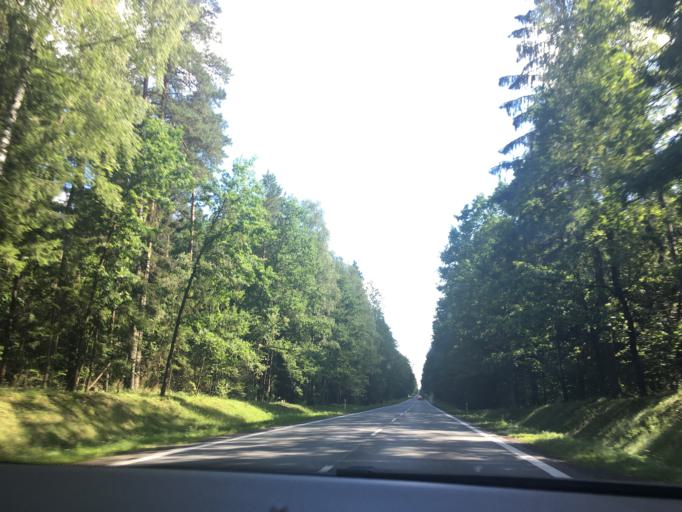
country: PL
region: Podlasie
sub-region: Powiat bialostocki
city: Wasilkow
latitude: 53.2991
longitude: 23.1245
